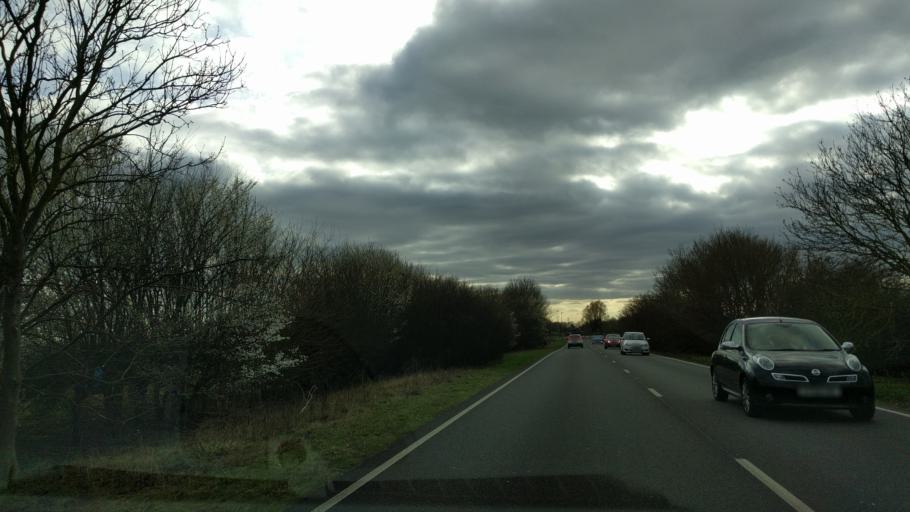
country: GB
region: England
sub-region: Cambridgeshire
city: Hemingford Grey
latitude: 52.3560
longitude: -0.1298
